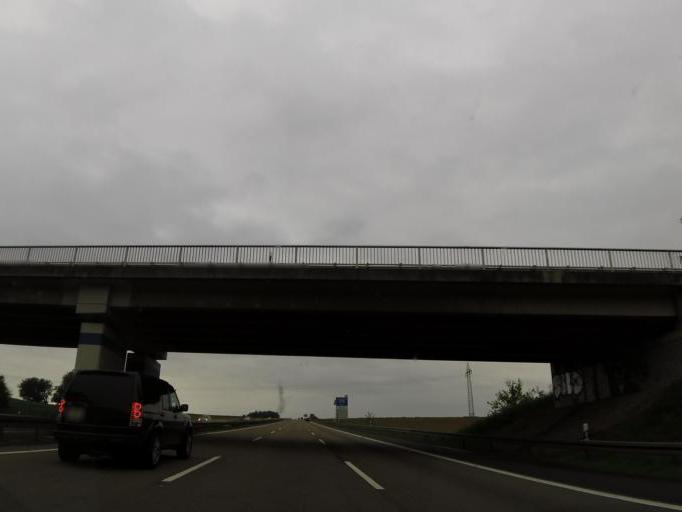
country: DE
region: Hesse
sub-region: Regierungsbezirk Kassel
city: Malsfeld
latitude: 51.0445
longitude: 9.4955
